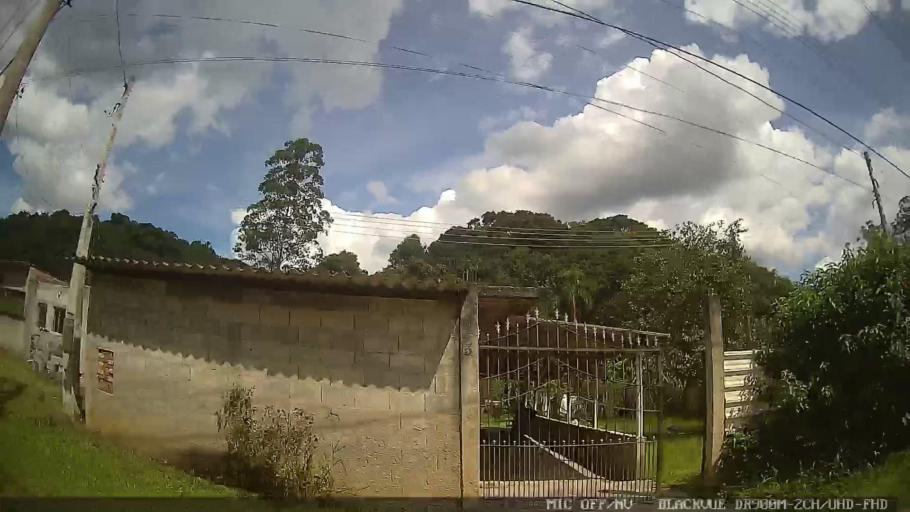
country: BR
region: Sao Paulo
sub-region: Suzano
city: Suzano
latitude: -23.6885
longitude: -46.2249
